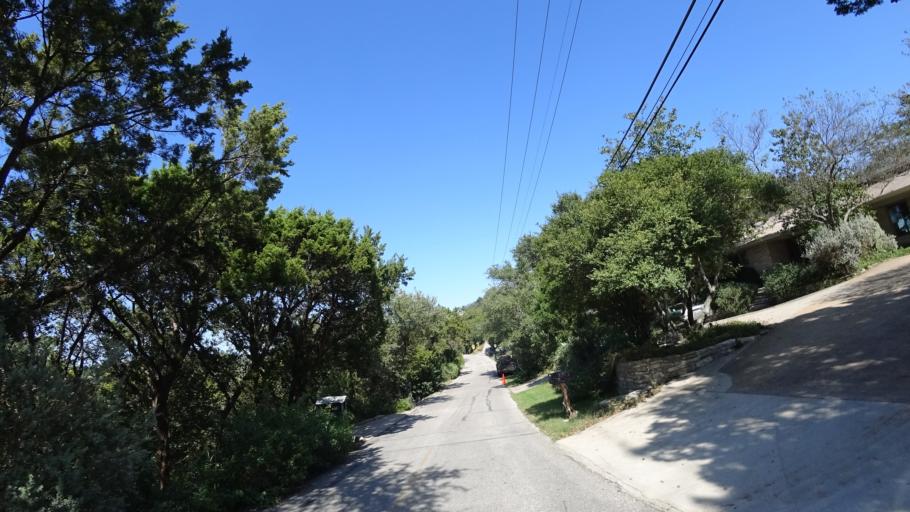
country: US
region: Texas
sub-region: Travis County
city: West Lake Hills
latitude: 30.3023
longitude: -97.8074
